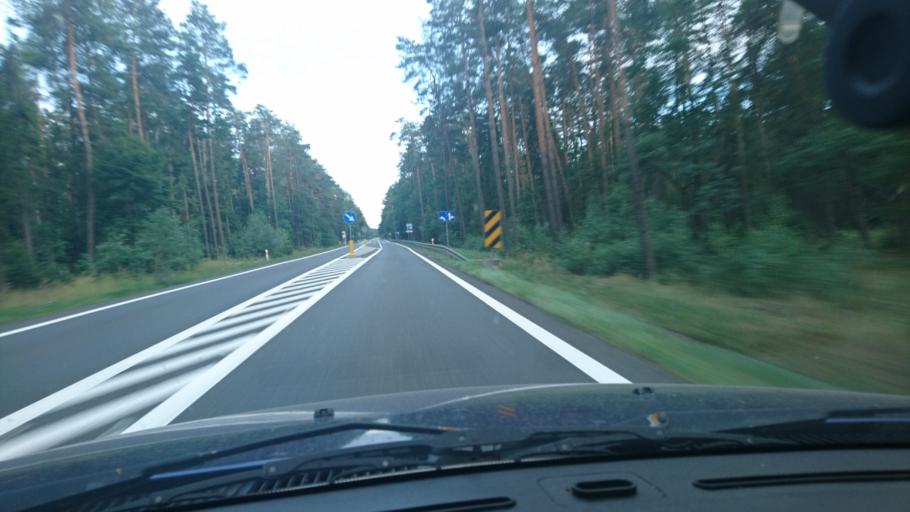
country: PL
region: Silesian Voivodeship
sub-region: Powiat lubliniecki
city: Lubliniec
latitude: 50.6126
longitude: 18.6925
